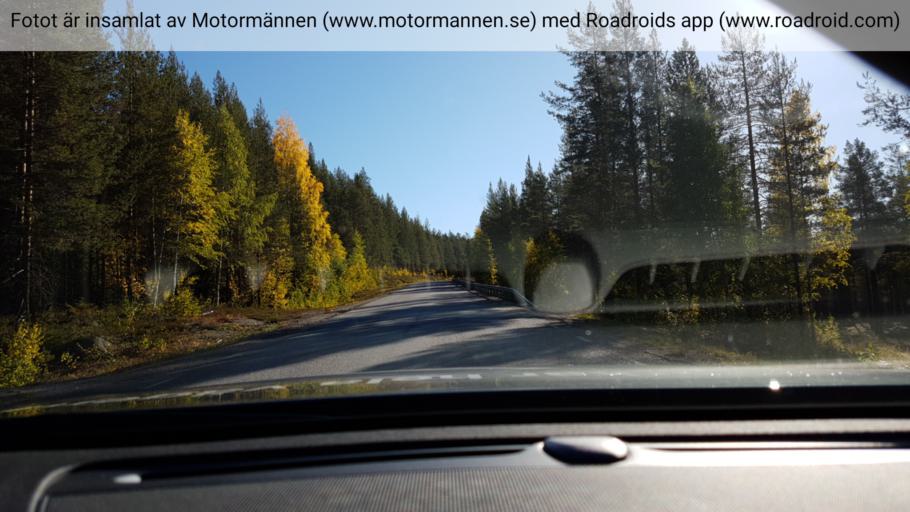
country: SE
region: Norrbotten
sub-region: Gallivare Kommun
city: Gaellivare
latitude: 66.4539
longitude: 20.6804
